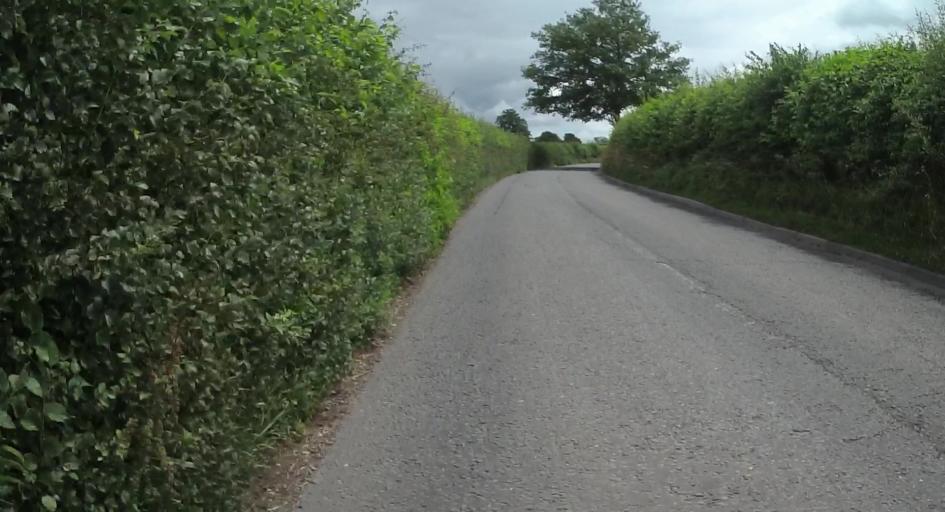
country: GB
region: England
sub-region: Surrey
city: Farnham
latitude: 51.2223
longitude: -0.8483
